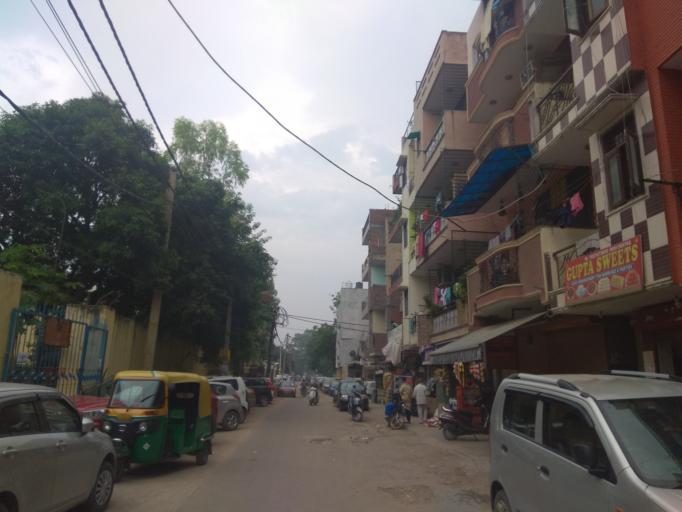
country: IN
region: NCT
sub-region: New Delhi
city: New Delhi
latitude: 28.5726
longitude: 77.2533
